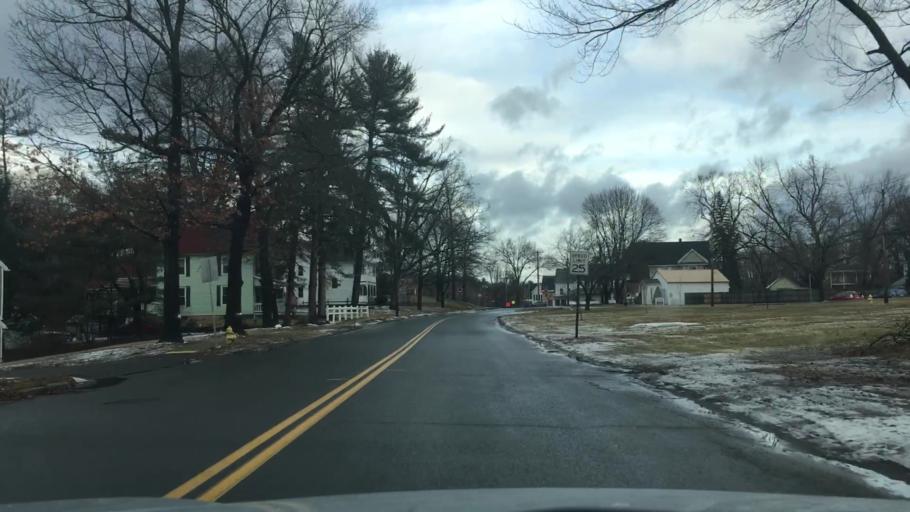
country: US
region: Massachusetts
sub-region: Franklin County
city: Greenfield
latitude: 42.6026
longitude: -72.6112
